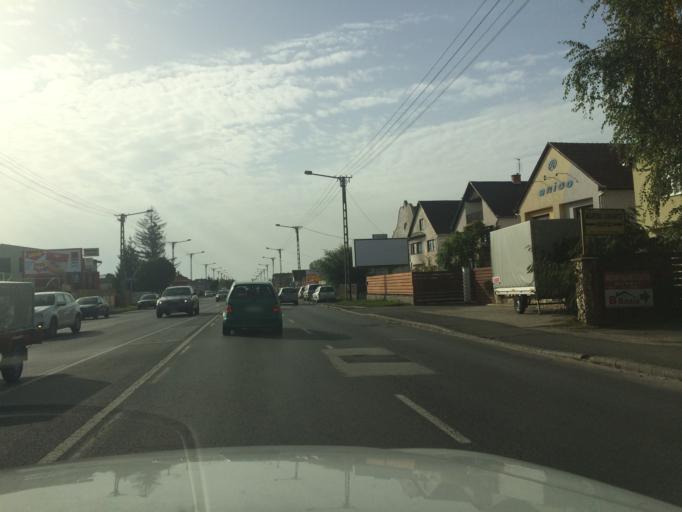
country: HU
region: Szabolcs-Szatmar-Bereg
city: Nyiregyhaza
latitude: 47.9318
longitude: 21.7187
